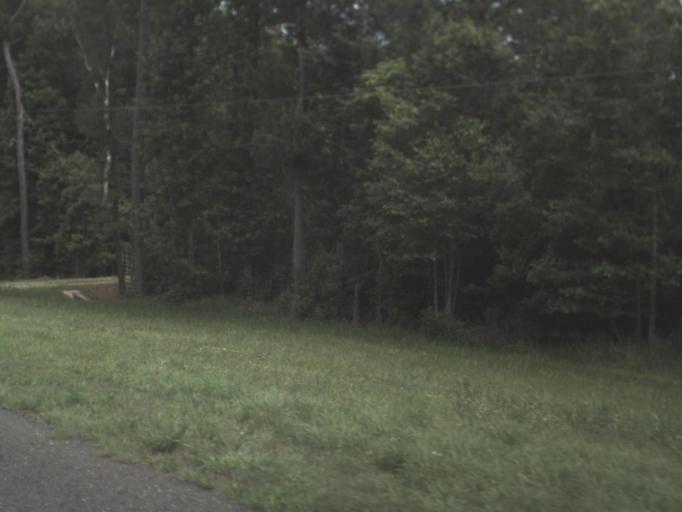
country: US
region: Florida
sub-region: Nassau County
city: Hilliard
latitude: 30.7579
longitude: -81.9643
